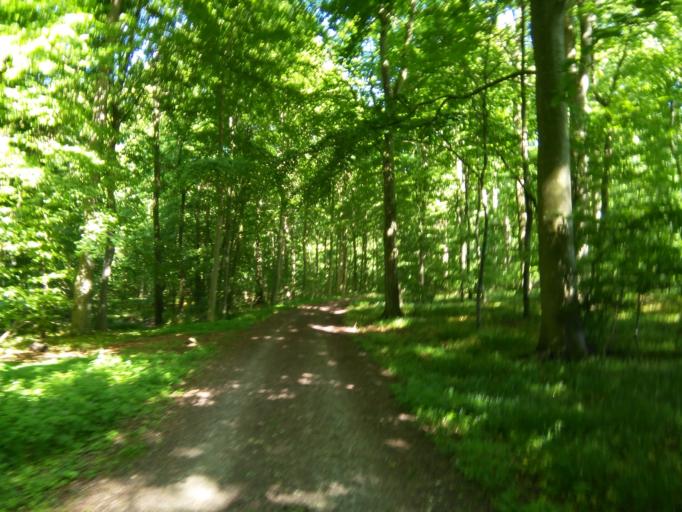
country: DK
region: Central Jutland
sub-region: Arhus Kommune
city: Marslet
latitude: 56.0253
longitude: 10.1565
